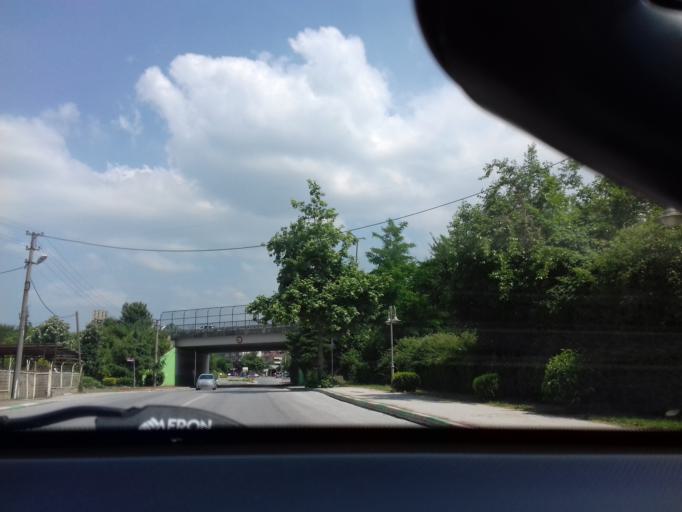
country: TR
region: Sakarya
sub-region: Merkez
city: Sapanca
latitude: 40.6891
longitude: 30.2777
